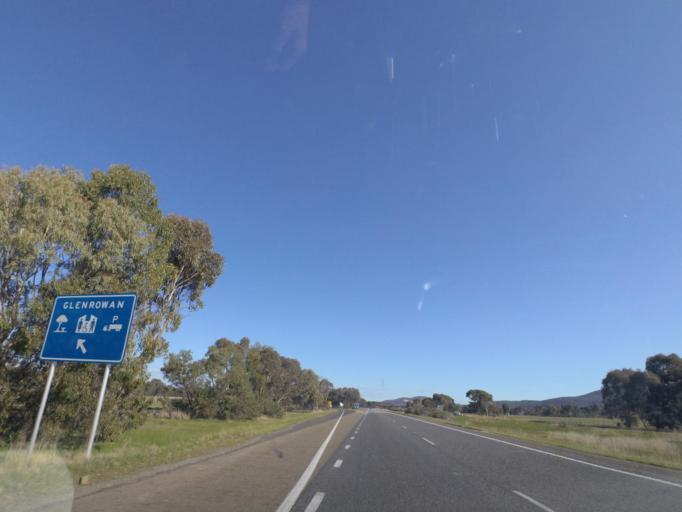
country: AU
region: Victoria
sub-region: Wangaratta
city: Wangaratta
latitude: -36.4207
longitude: 146.2644
